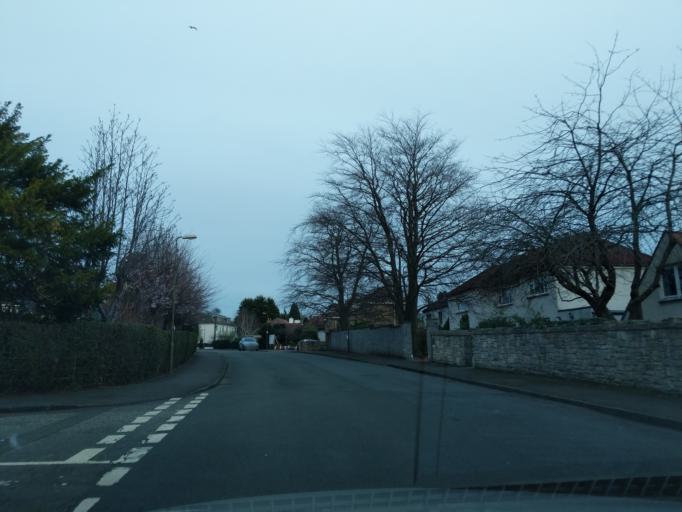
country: GB
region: Scotland
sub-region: Edinburgh
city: Currie
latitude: 55.9668
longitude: -3.3119
